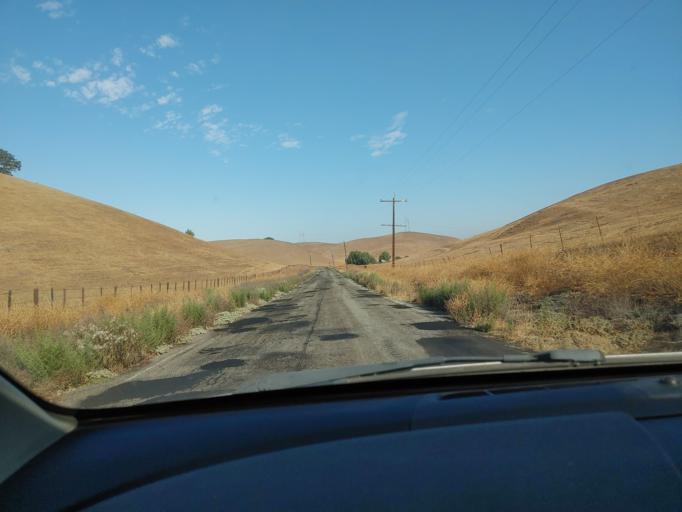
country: US
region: California
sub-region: San Benito County
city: Ridgemark
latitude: 36.8031
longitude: -121.2957
